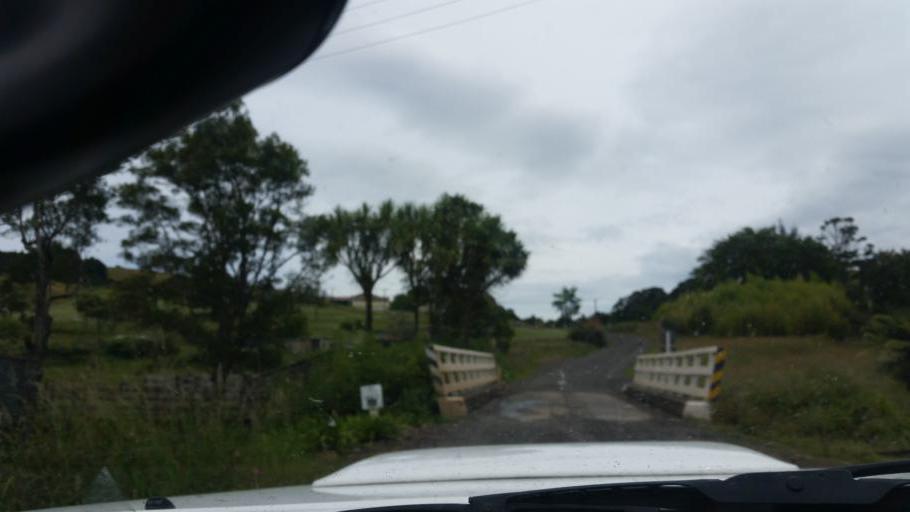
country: NZ
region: Northland
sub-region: Kaipara District
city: Dargaville
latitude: -35.7110
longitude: 173.6153
